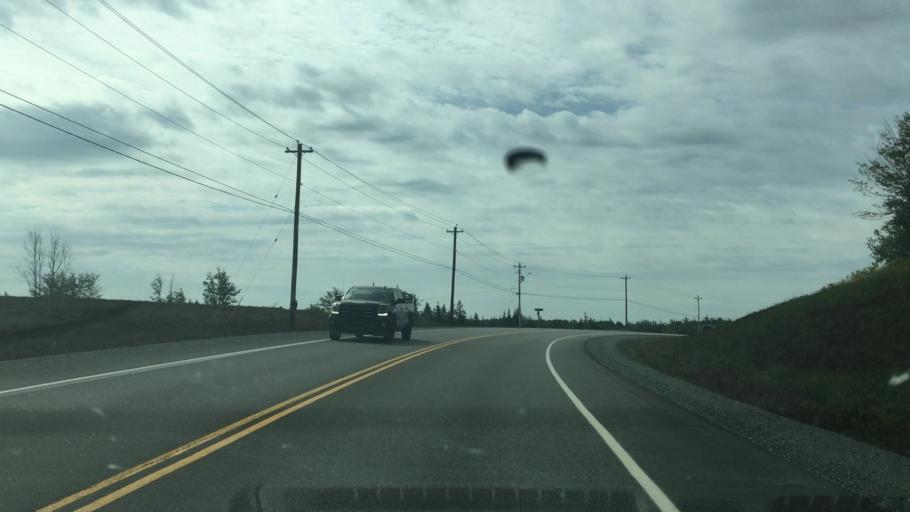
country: CA
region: Nova Scotia
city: Princeville
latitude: 45.6613
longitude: -60.8136
